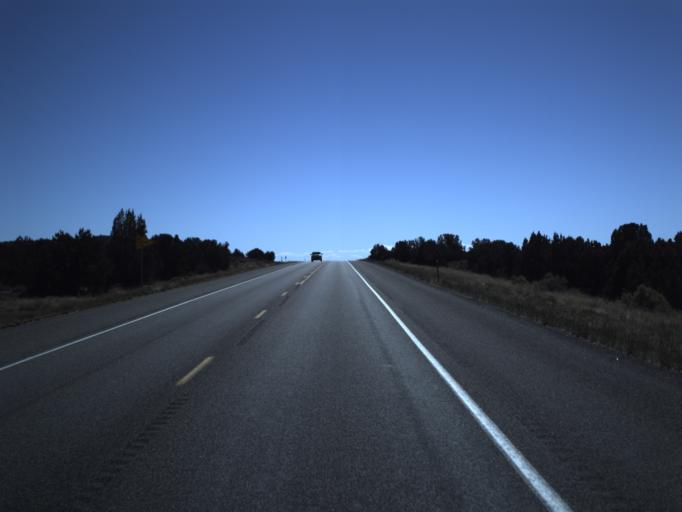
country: US
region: Utah
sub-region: Washington County
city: Ivins
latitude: 37.2907
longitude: -113.6601
